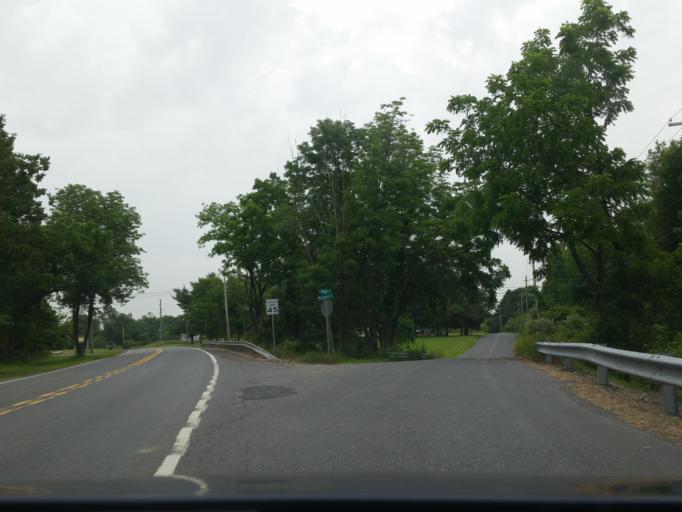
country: US
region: Pennsylvania
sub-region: Dauphin County
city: Skyline View
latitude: 40.4012
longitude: -76.6547
